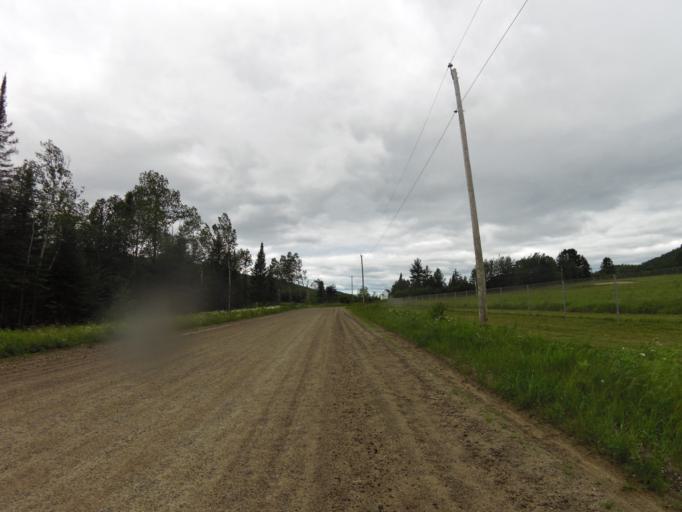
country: CA
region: Quebec
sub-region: Laurentides
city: Mont-Tremblant
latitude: 45.9128
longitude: -74.6526
